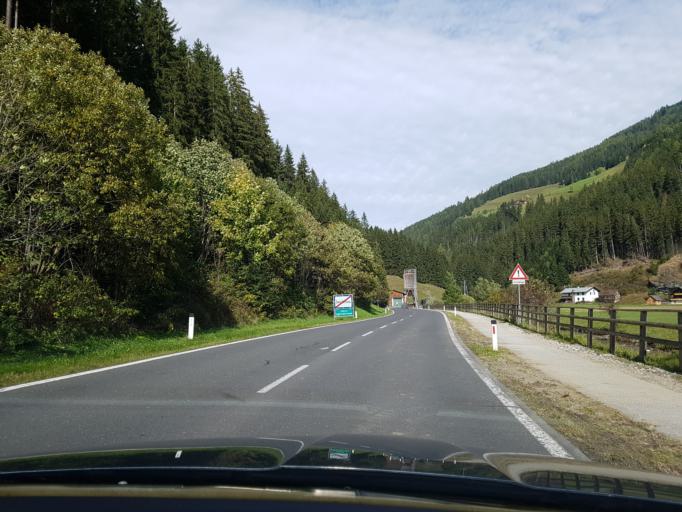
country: AT
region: Carinthia
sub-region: Politischer Bezirk Spittal an der Drau
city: Kleinkirchheim
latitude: 46.8590
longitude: 13.8909
